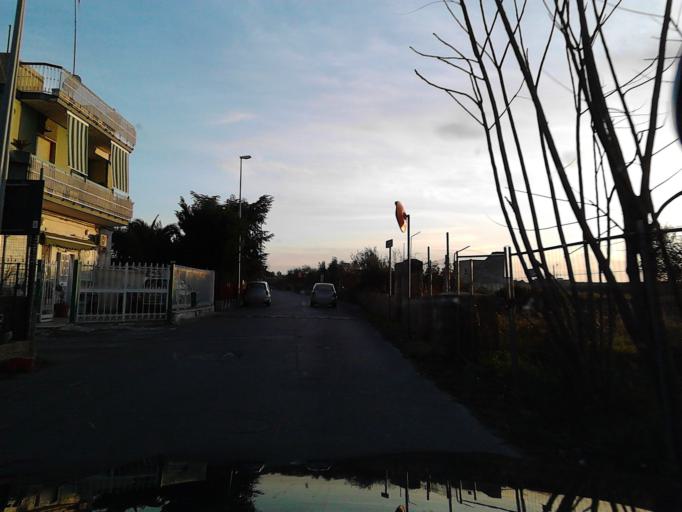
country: IT
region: Apulia
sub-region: Provincia di Bari
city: Triggiano
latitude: 41.0586
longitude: 16.9217
